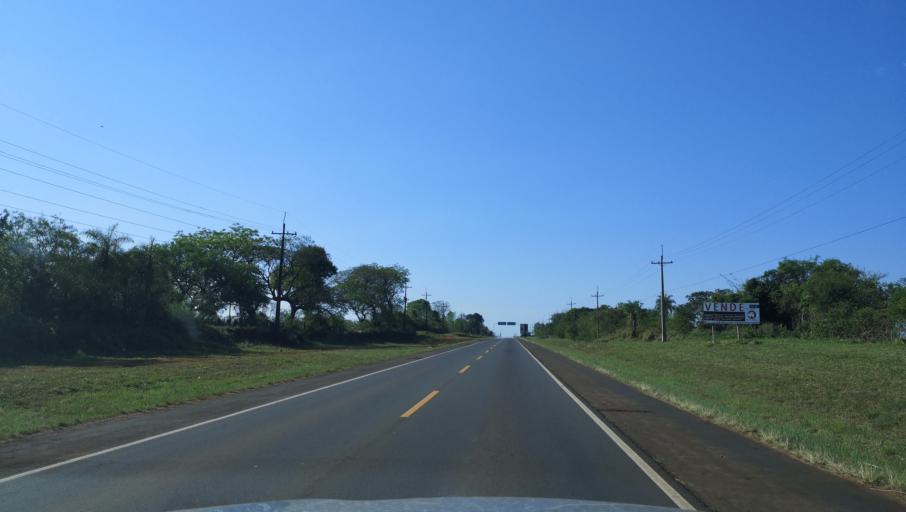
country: PY
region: Misiones
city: Santa Rosa
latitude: -26.9092
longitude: -56.8588
